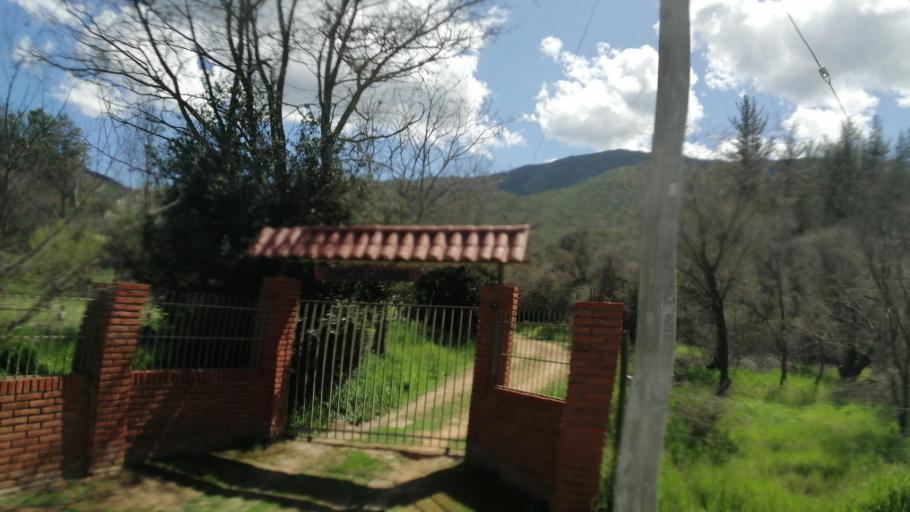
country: CL
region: Valparaiso
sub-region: Provincia de Marga Marga
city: Limache
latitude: -33.1859
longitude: -71.1906
